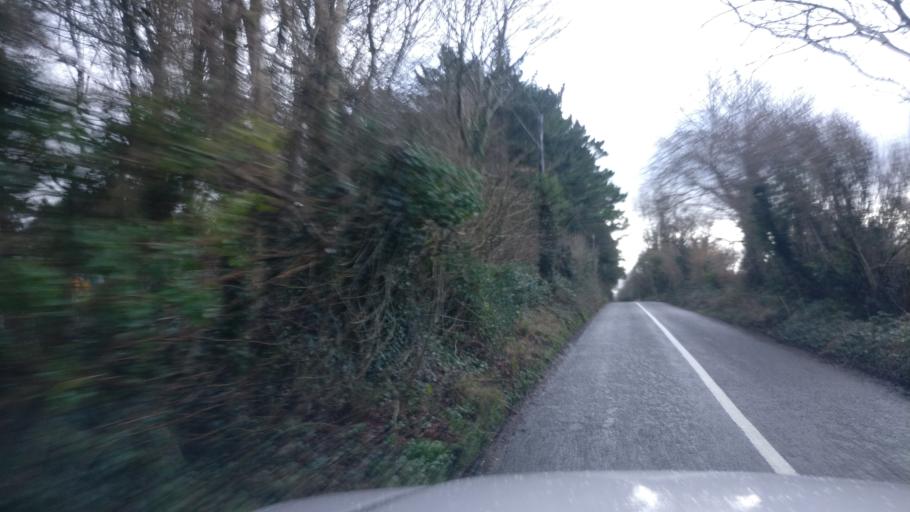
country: IE
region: Connaught
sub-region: County Galway
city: Loughrea
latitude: 53.2486
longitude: -8.6225
